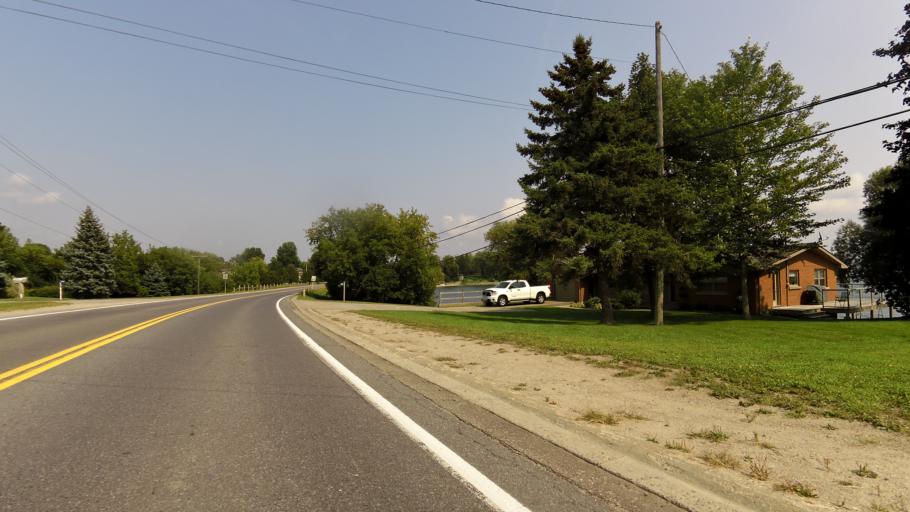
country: CA
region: Ontario
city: Prescott
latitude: 44.6977
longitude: -75.5380
